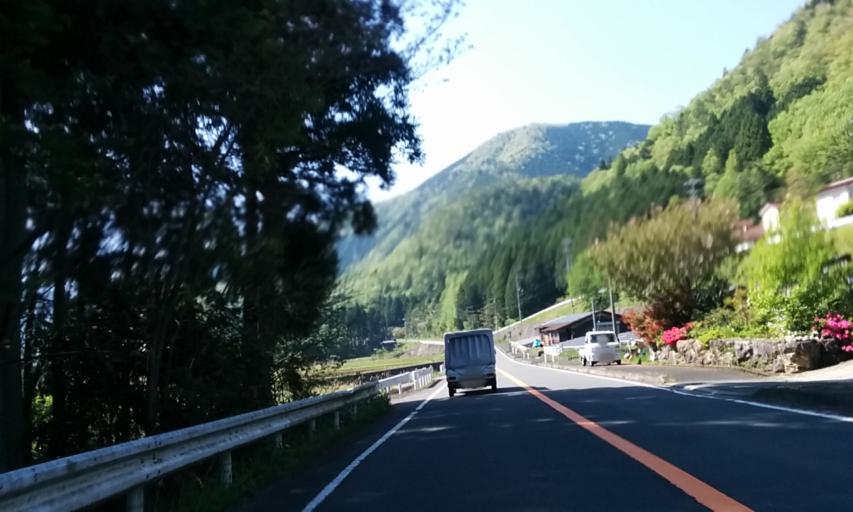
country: JP
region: Kyoto
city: Maizuru
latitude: 35.2778
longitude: 135.5425
